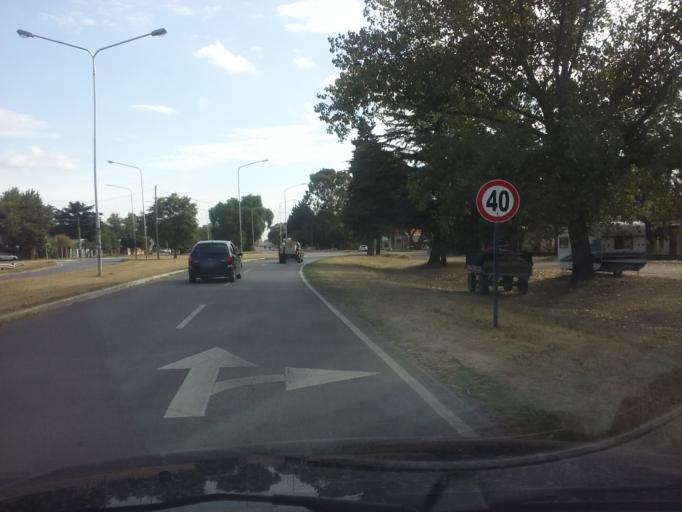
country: AR
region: La Pampa
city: Santa Rosa
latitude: -36.6399
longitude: -64.3221
